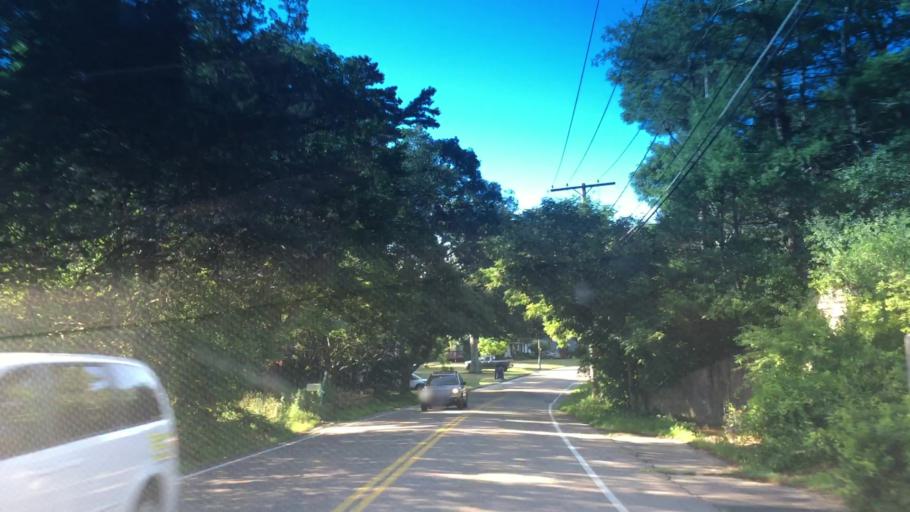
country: US
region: Massachusetts
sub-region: Norfolk County
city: Medway
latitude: 42.1488
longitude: -71.3915
